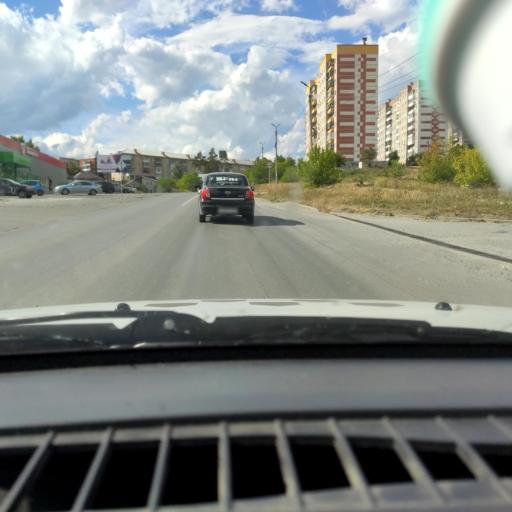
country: RU
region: Chelyabinsk
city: Miass
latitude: 55.0753
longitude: 60.0947
